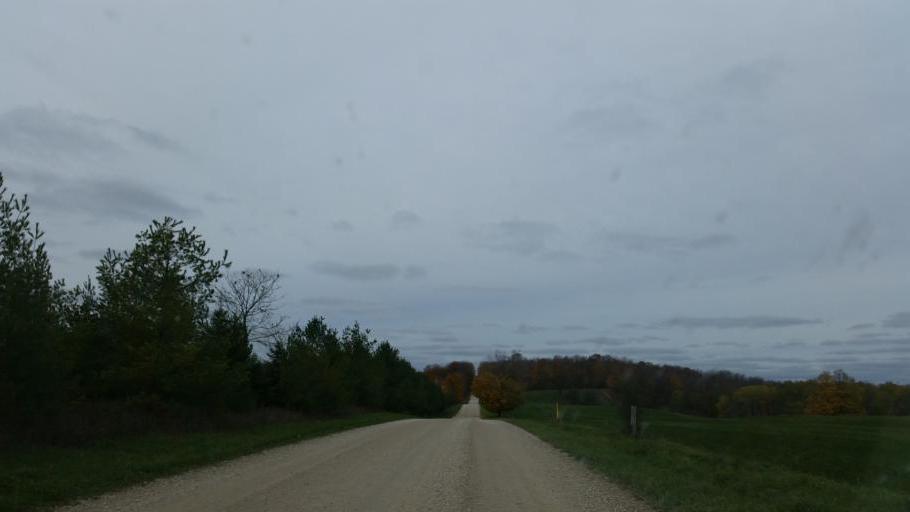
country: CA
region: Ontario
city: Wingham
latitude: 43.9794
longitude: -81.3333
